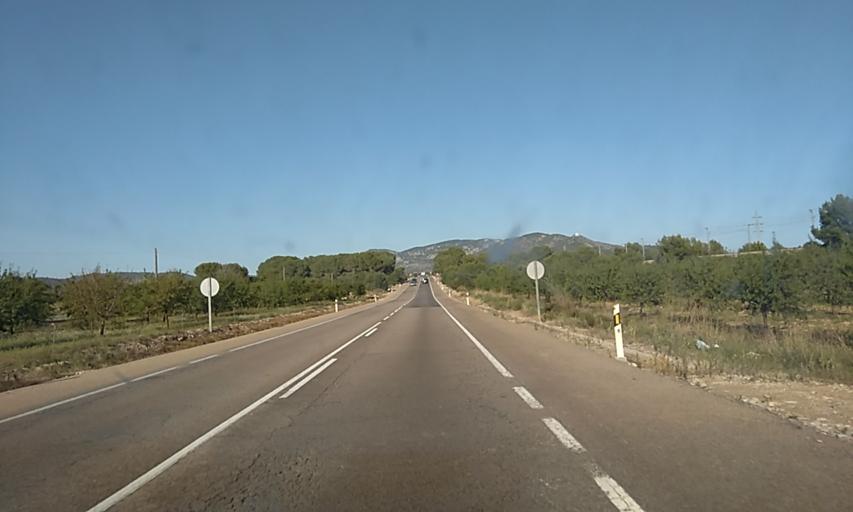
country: ES
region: Valencia
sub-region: Provincia de Castello
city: Torreblanca
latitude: 40.2403
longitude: 0.2267
